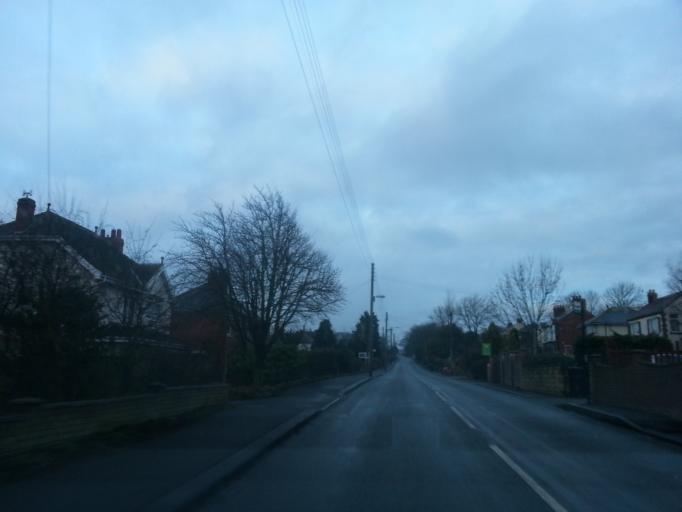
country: GB
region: England
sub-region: County Durham
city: Crook
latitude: 54.7121
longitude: -1.7585
